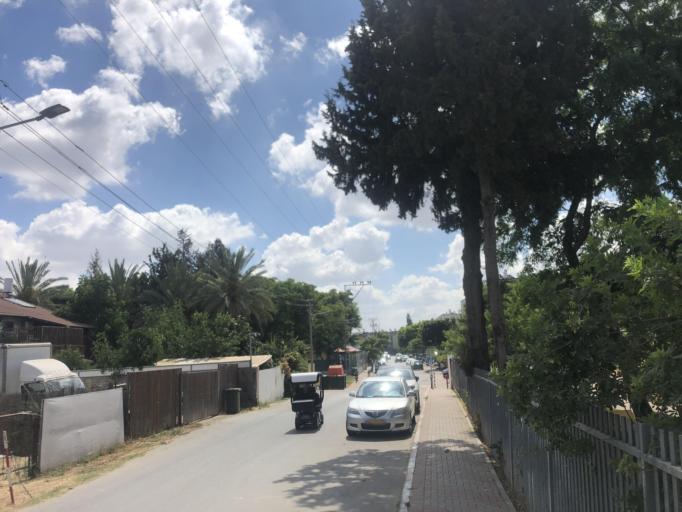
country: IL
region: Central District
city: Yehud
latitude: 32.0305
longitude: 34.8942
